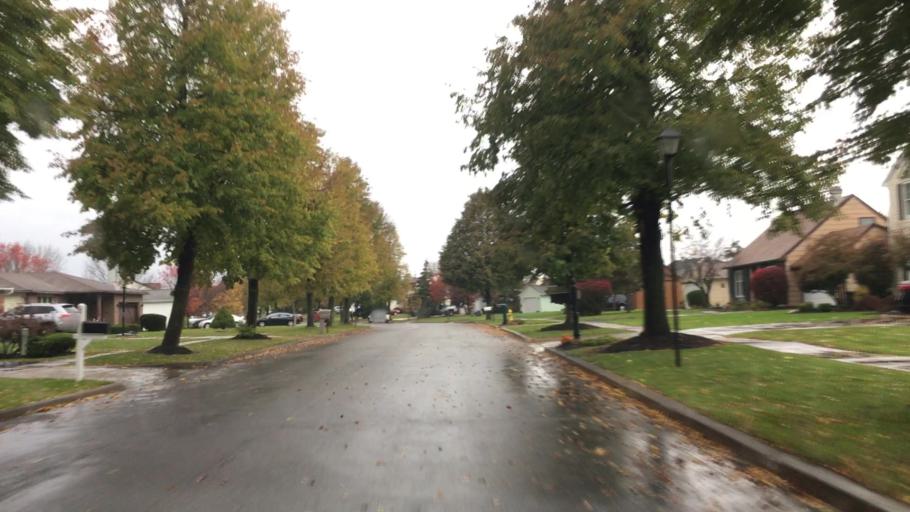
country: US
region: New York
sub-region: Erie County
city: Lancaster
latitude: 42.8753
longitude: -78.6790
